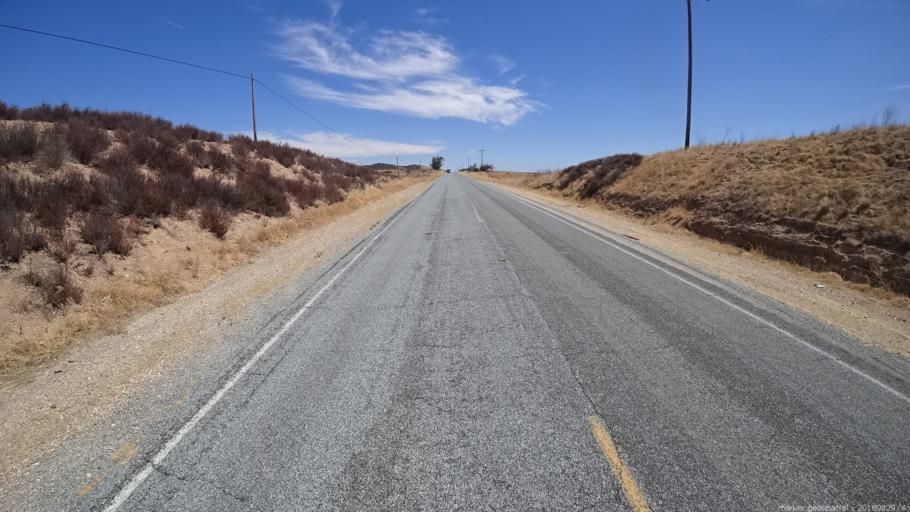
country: US
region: California
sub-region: San Luis Obispo County
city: Lake Nacimiento
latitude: 35.9280
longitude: -121.0479
